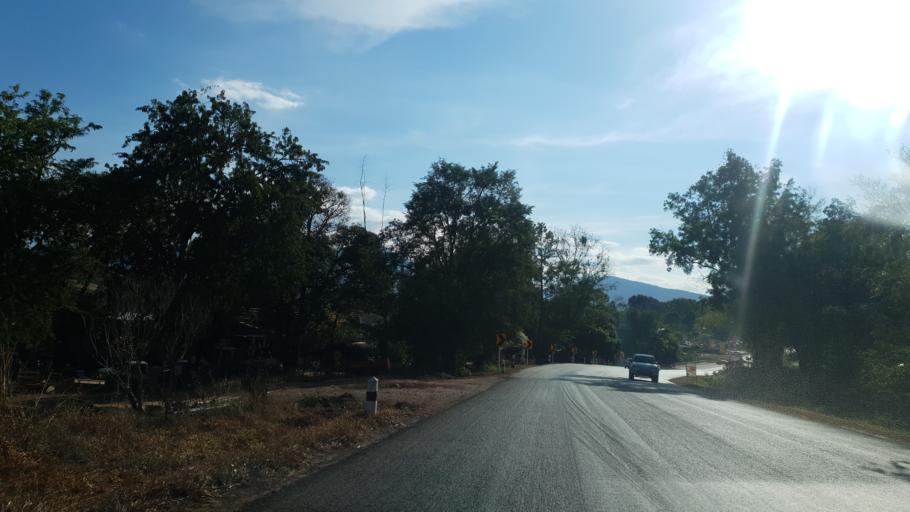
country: TH
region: Loei
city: Phu Ruea
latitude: 17.4442
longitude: 101.4747
